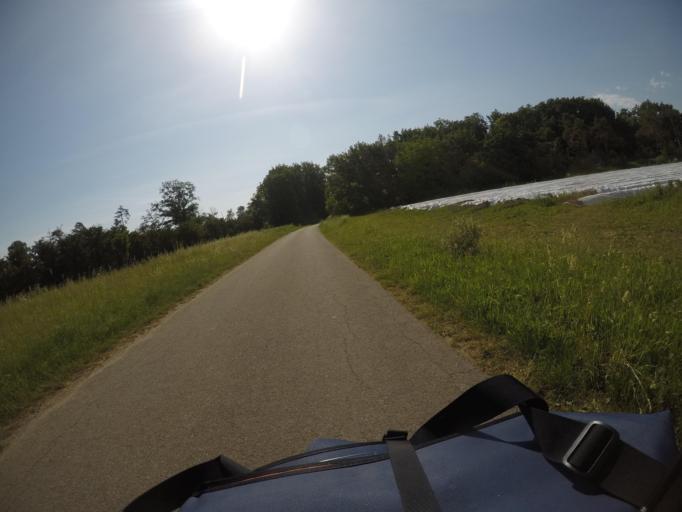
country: DE
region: Baden-Wuerttemberg
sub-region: Karlsruhe Region
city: Durmersheim
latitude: 48.9086
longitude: 8.2823
